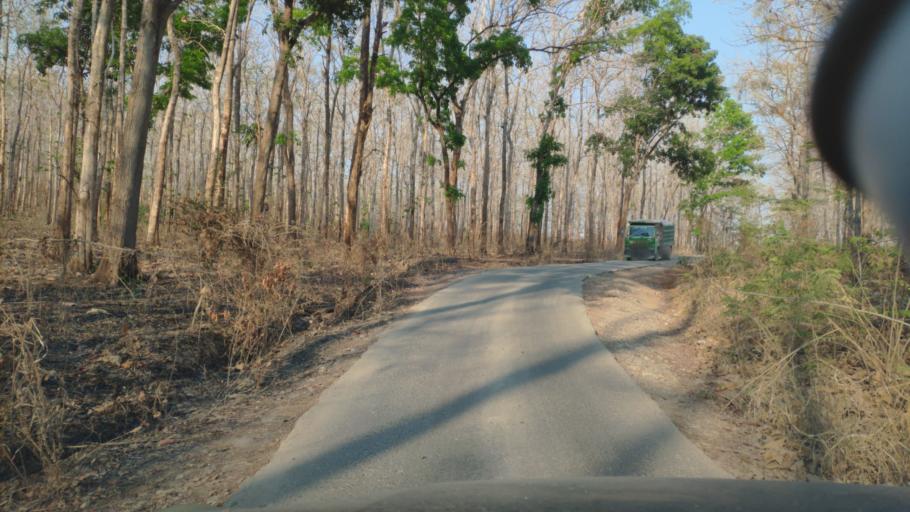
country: ID
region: Central Java
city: Sendangrejo
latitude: -6.9175
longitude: 111.5523
